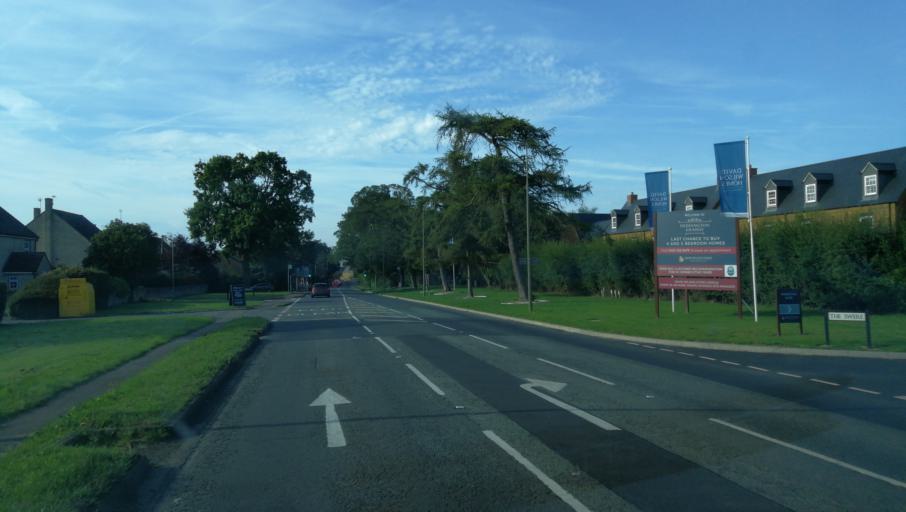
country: GB
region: England
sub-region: Oxfordshire
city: Deddington
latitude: 51.9847
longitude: -1.3226
